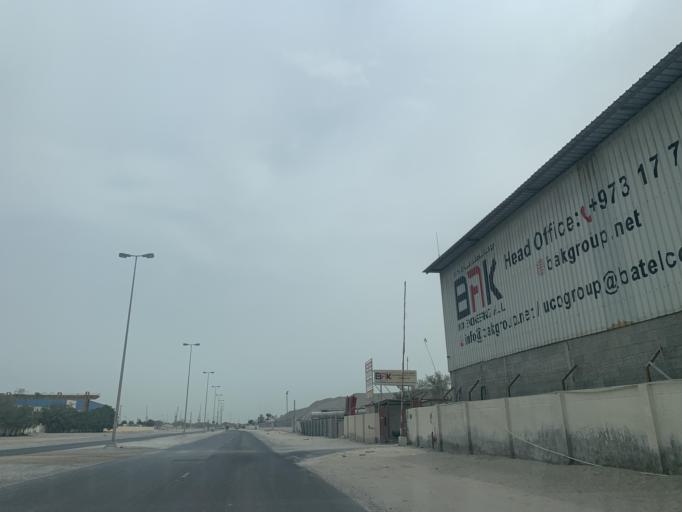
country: BH
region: Muharraq
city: Al Hadd
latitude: 26.2079
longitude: 50.6590
